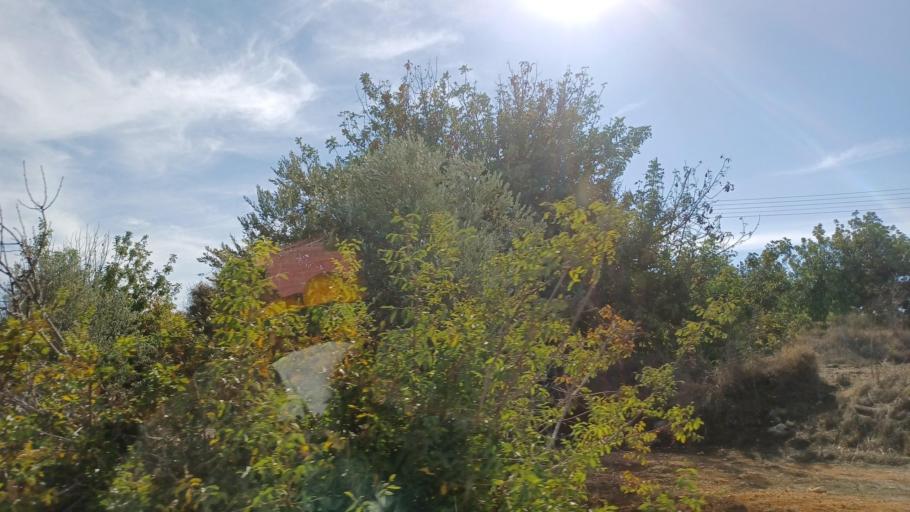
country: CY
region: Pafos
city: Pegeia
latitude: 34.9422
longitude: 32.4509
